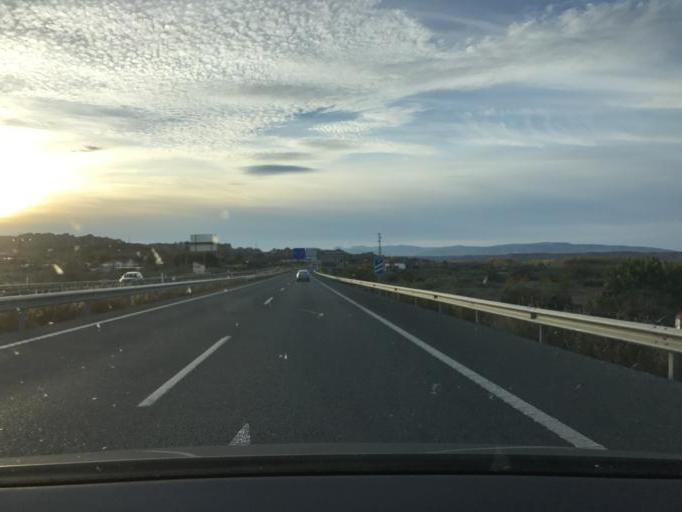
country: ES
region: Andalusia
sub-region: Provincia de Granada
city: Guadix
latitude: 37.3198
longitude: -3.1462
